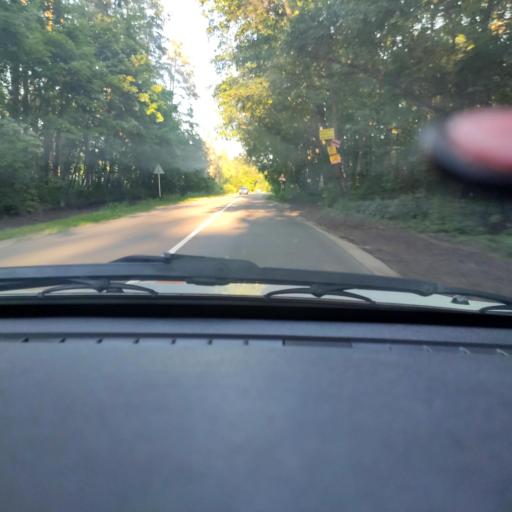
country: RU
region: Voronezj
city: Ramon'
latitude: 51.8932
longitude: 39.2281
